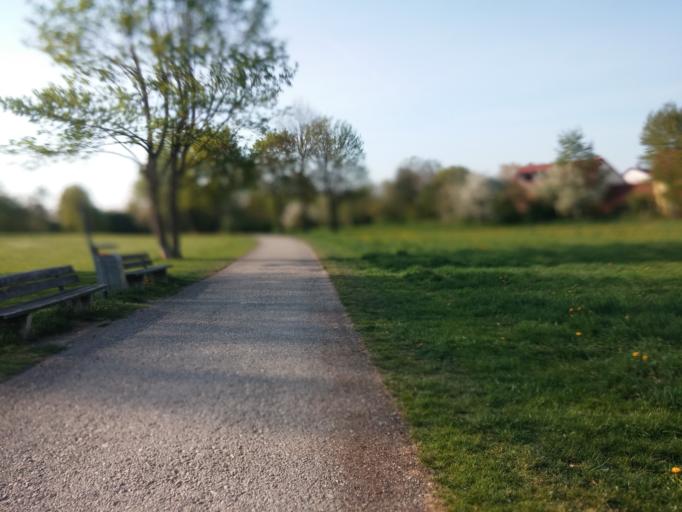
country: DE
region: Bavaria
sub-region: Upper Bavaria
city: Neubiberg
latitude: 48.1077
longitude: 11.6614
